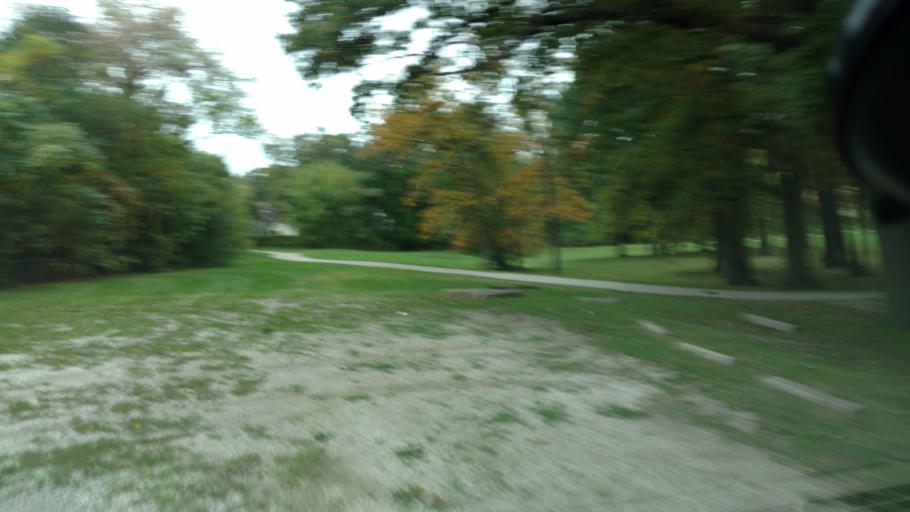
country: US
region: Michigan
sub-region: Ingham County
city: Lansing
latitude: 42.7271
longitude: -84.5312
